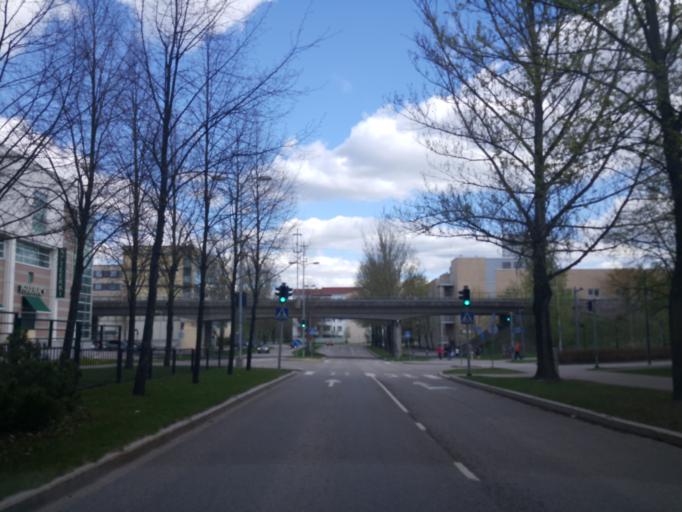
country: FI
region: Uusimaa
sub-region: Helsinki
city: Teekkarikylae
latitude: 60.2591
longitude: 24.8534
